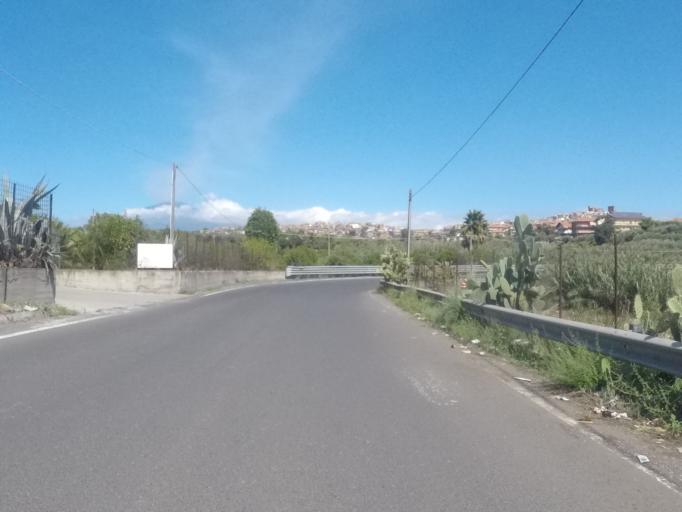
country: IT
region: Sicily
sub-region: Catania
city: Motta Sant'Anastasia
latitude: 37.5036
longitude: 14.9595
